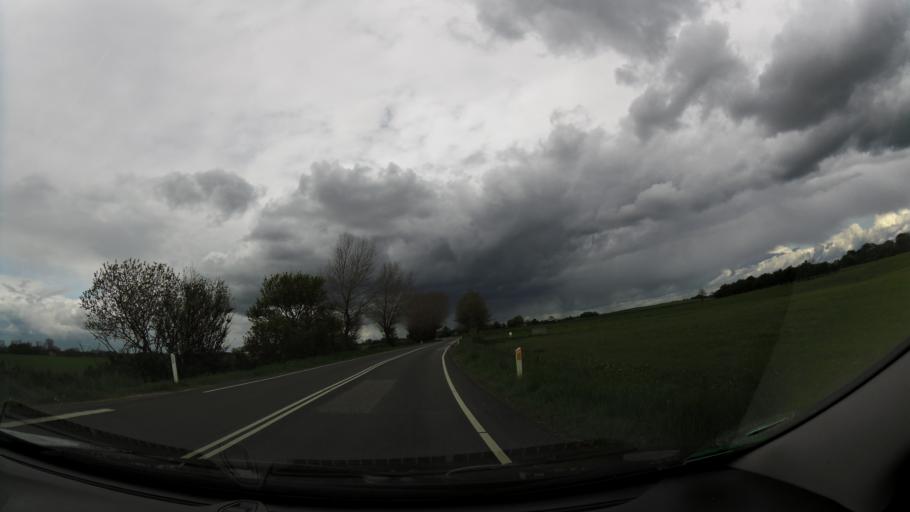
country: DK
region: South Denmark
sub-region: Svendborg Kommune
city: Thuro By
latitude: 55.1755
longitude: 10.7329
